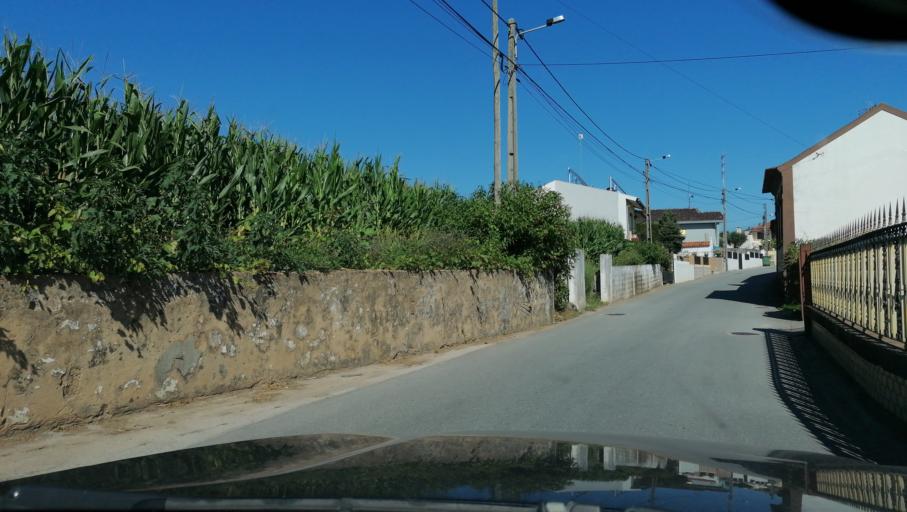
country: PT
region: Aveiro
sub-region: Estarreja
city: Salreu
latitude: 40.7497
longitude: -8.5541
